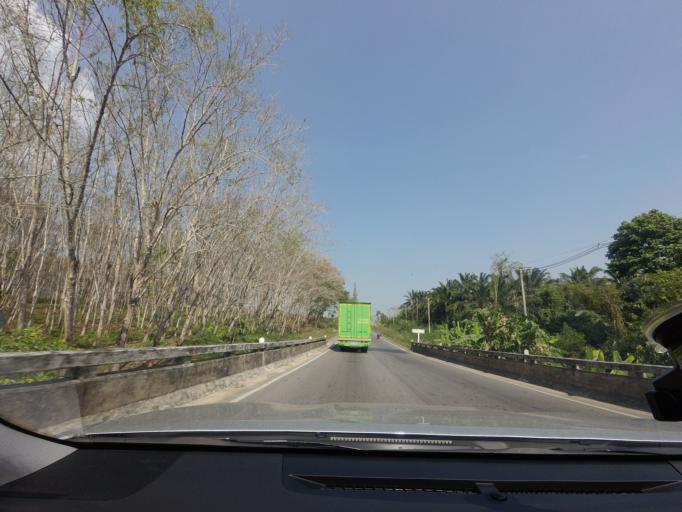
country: TH
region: Krabi
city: Plai Phraya
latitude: 8.5567
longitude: 98.8039
